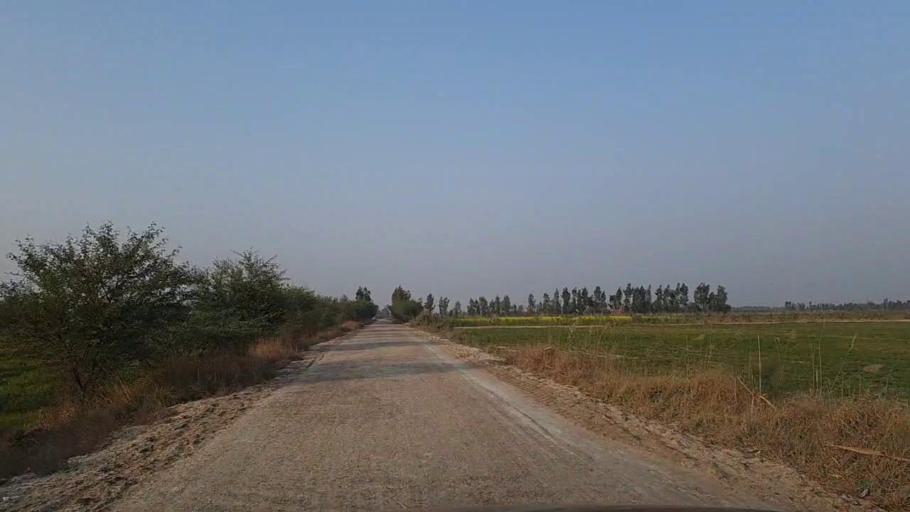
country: PK
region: Sindh
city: Daur
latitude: 26.4196
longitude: 68.3935
